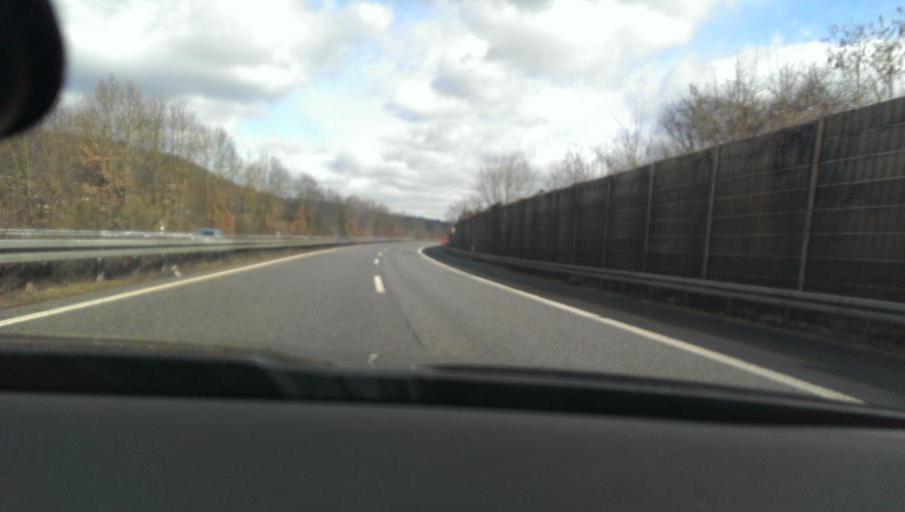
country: DE
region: Hesse
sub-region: Regierungsbezirk Darmstadt
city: Gelnhausen
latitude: 50.2052
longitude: 9.2280
